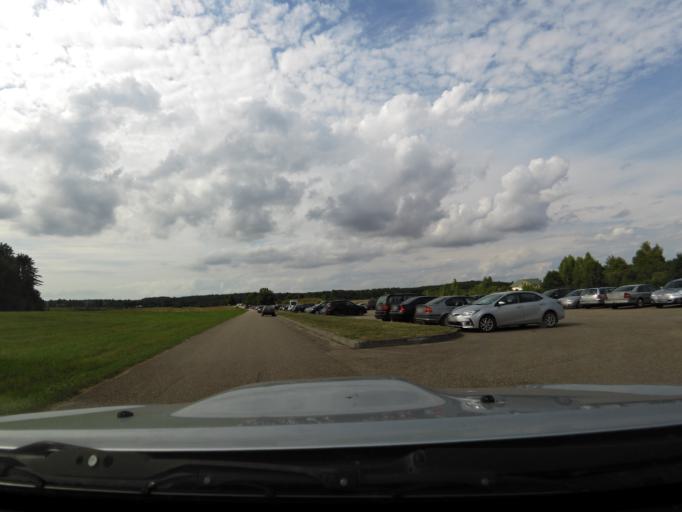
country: LT
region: Vilnius County
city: Elektrenai
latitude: 54.8373
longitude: 24.5668
